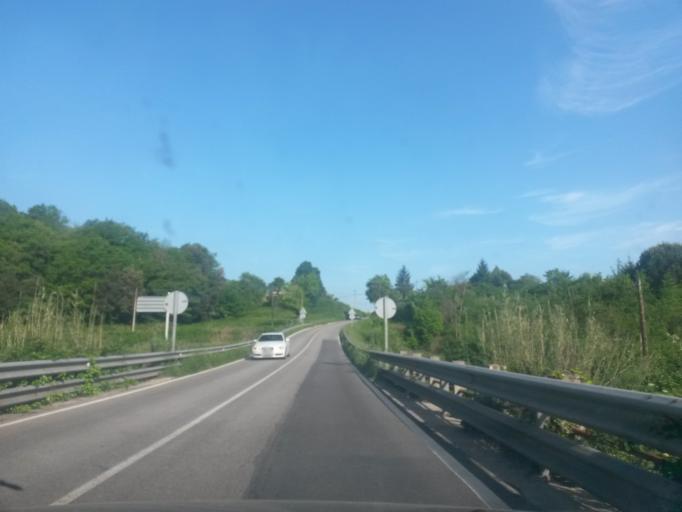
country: ES
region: Catalonia
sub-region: Provincia de Girona
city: les Planes d'Hostoles
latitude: 42.0498
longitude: 2.5501
